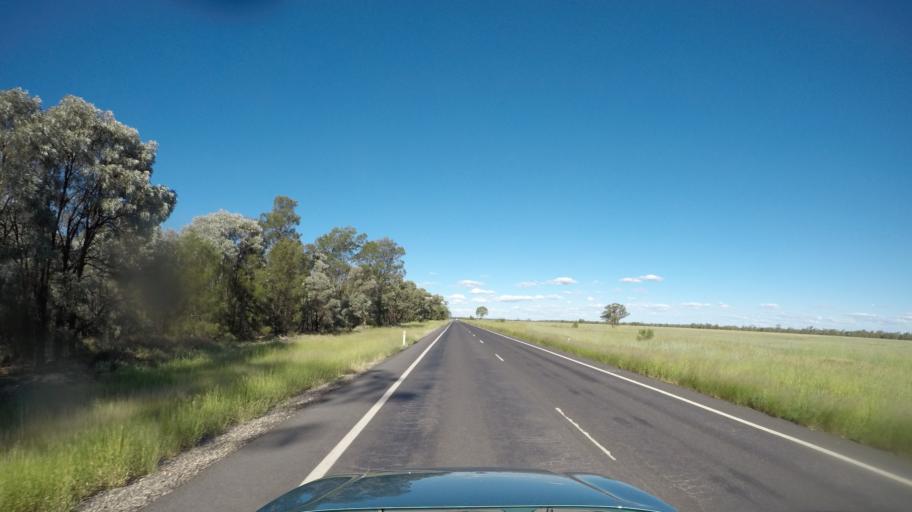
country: AU
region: Queensland
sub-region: Goondiwindi
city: Goondiwindi
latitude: -28.1548
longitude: 150.6738
